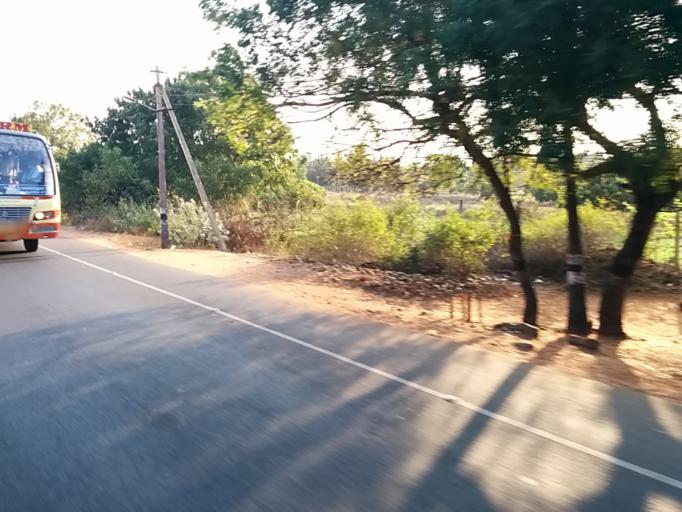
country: IN
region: Tamil Nadu
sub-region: Villupuram
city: Auroville
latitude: 11.9988
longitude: 79.8521
